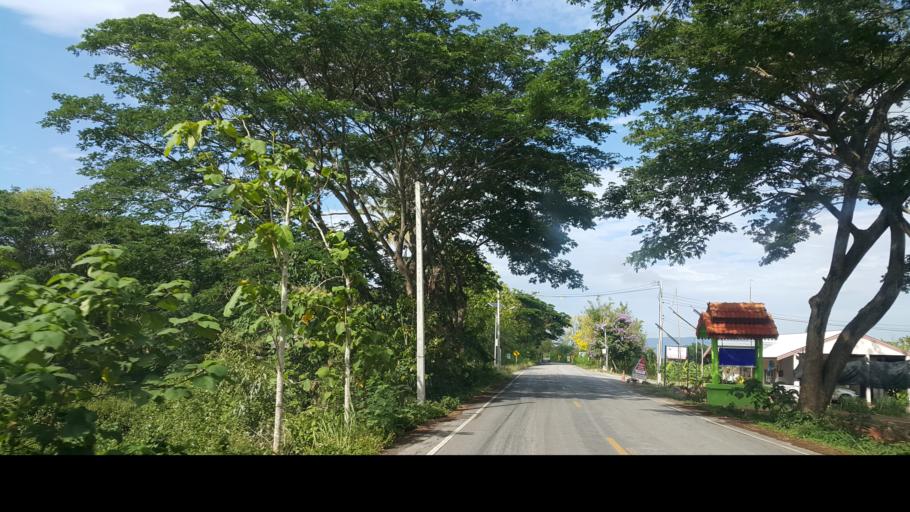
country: TH
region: Chiang Rai
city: Wiang Chai
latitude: 19.9388
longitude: 99.9178
